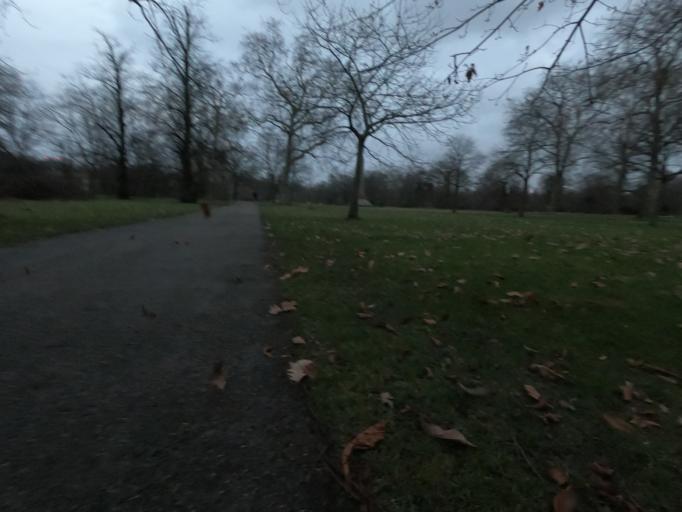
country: GB
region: England
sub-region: Greater London
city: Bayswater
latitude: 51.5087
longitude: -0.1801
